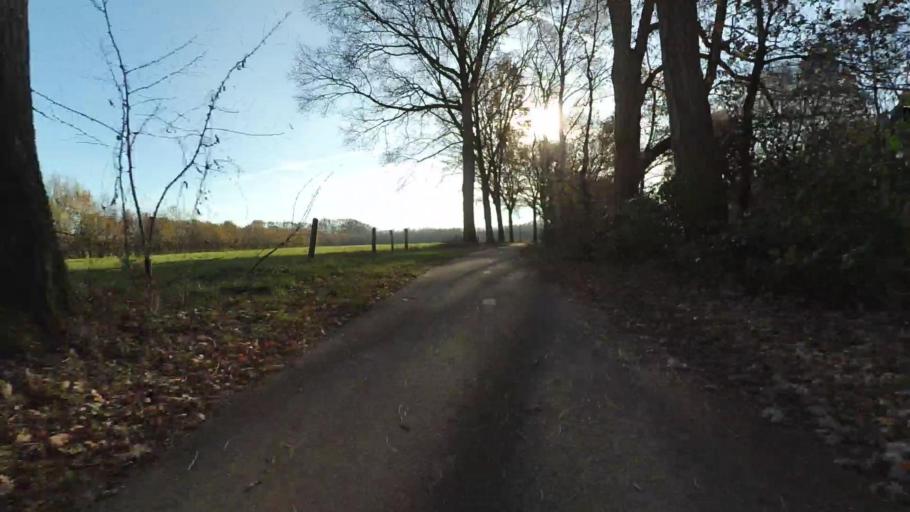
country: NL
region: Utrecht
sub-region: Gemeente Utrechtse Heuvelrug
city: Overberg
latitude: 52.0713
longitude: 5.4776
